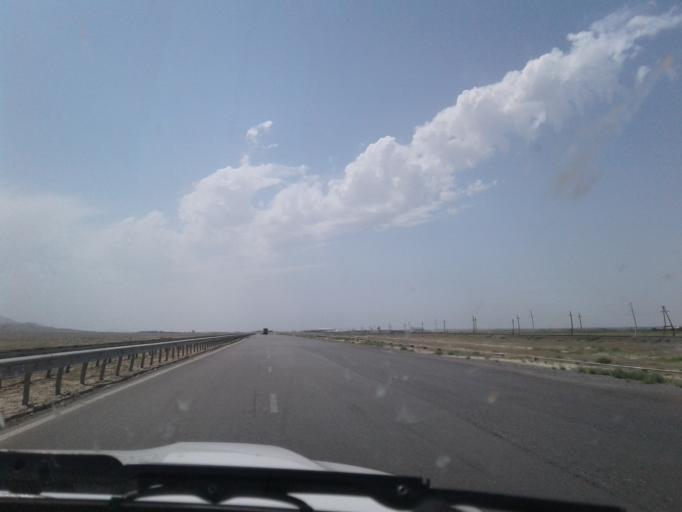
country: IR
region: Razavi Khorasan
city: Dargaz
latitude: 37.7542
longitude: 58.9412
